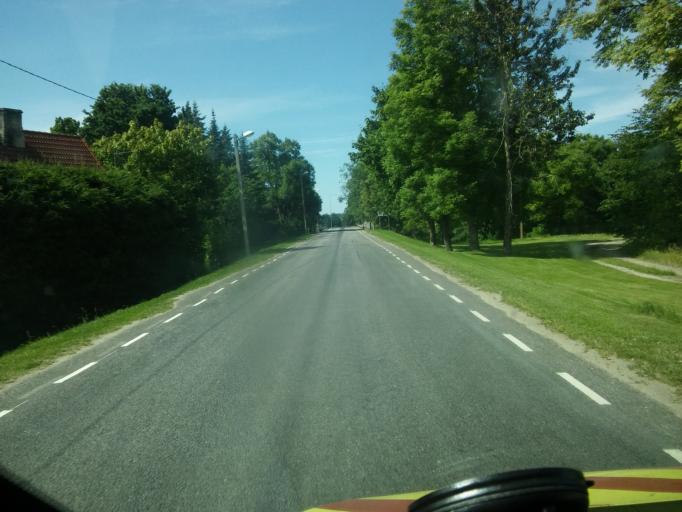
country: EE
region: Paernumaa
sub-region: Paikuse vald
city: Paikuse
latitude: 58.2375
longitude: 24.7058
